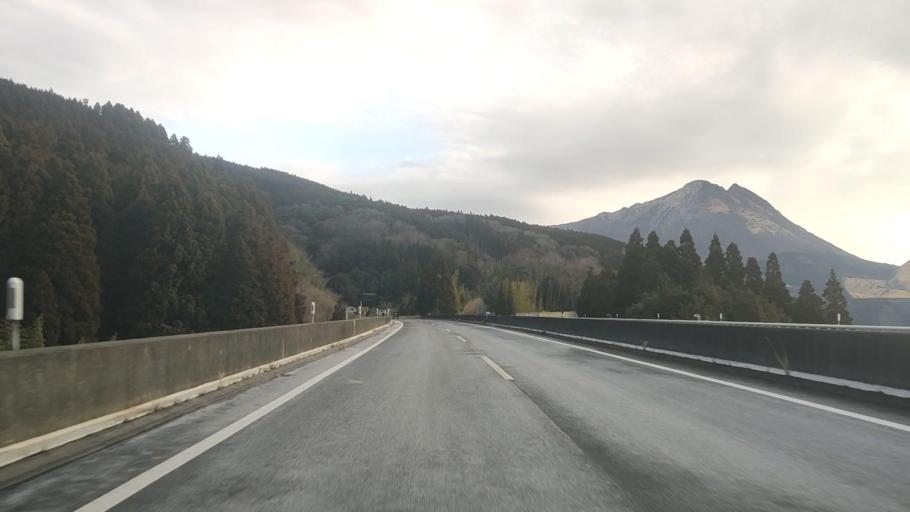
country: JP
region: Oita
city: Beppu
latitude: 33.2654
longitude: 131.3364
